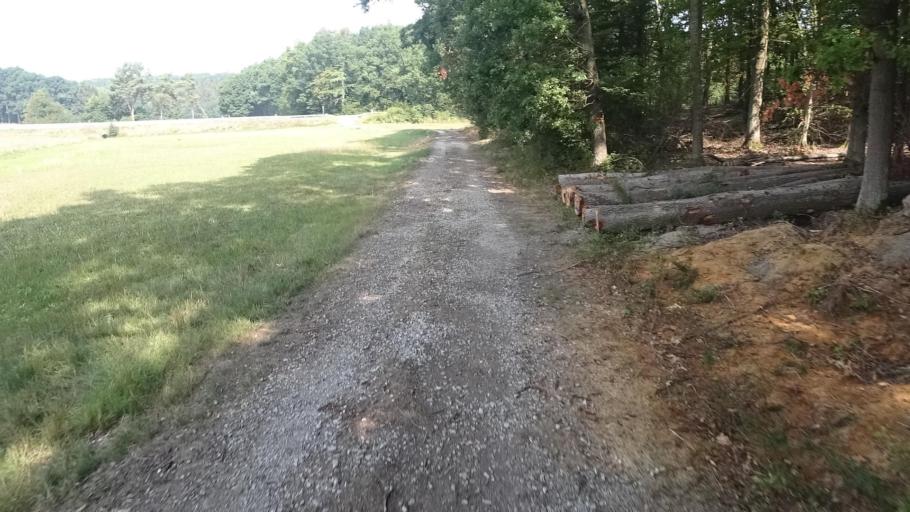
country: DE
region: Rheinland-Pfalz
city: Mutterschied
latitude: 49.9916
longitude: 7.5538
